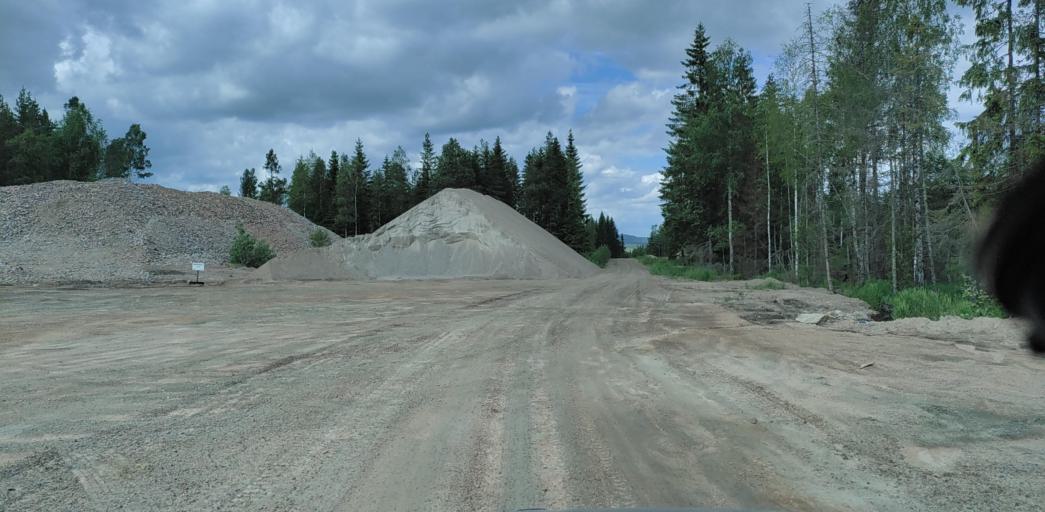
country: SE
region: Vaermland
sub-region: Munkfors Kommun
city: Munkfors
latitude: 59.9548
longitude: 13.4104
